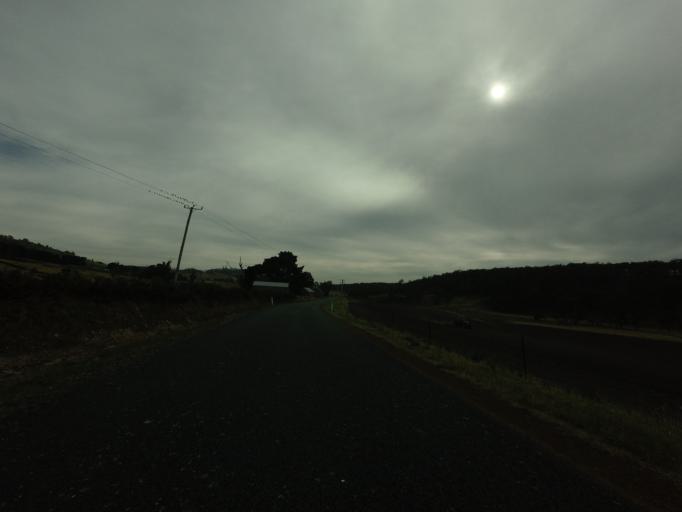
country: AU
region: Tasmania
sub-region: Sorell
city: Sorell
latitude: -42.4657
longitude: 147.5690
